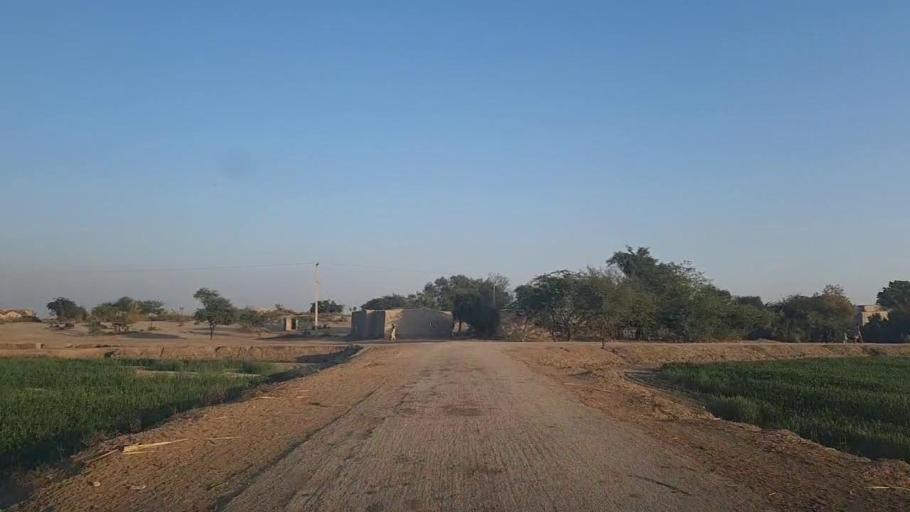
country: PK
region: Sindh
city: Jam Sahib
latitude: 26.3339
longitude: 68.6978
